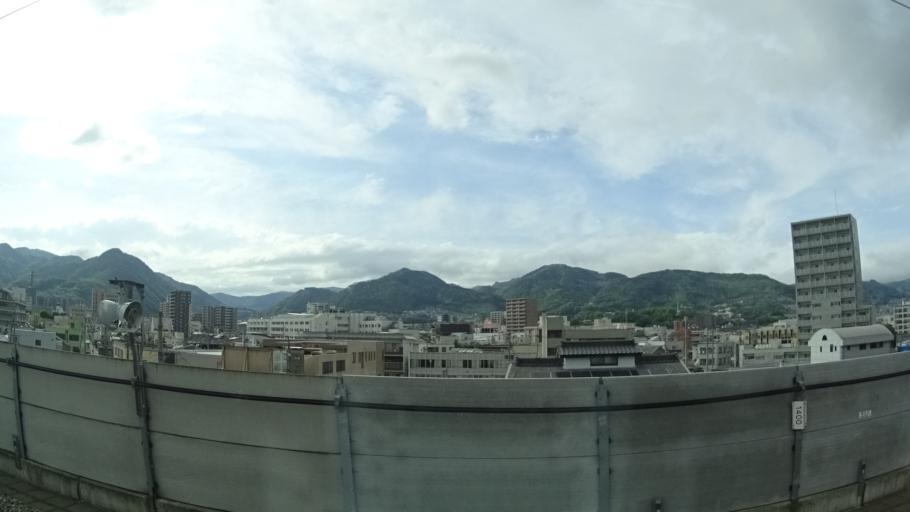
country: JP
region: Nagano
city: Nagano-shi
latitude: 36.6502
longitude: 138.1988
